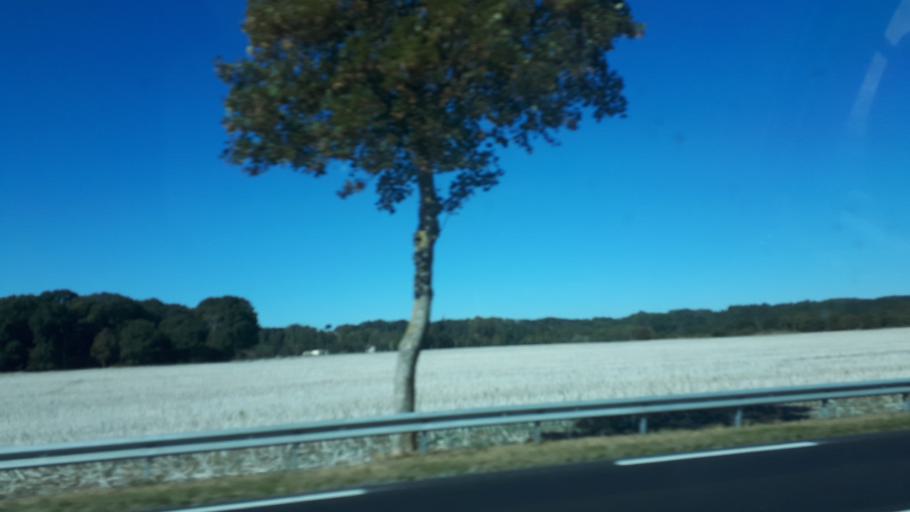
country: FR
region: Centre
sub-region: Departement d'Eure-et-Loir
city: Marboue
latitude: 48.1032
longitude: 1.3300
